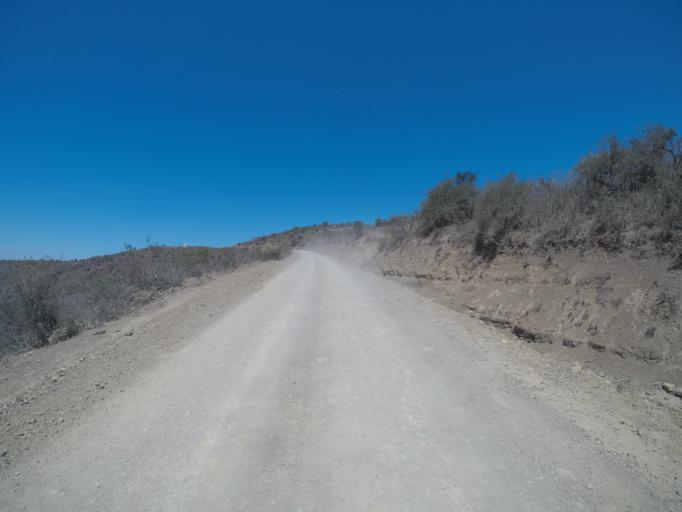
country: ZA
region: Eastern Cape
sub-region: OR Tambo District Municipality
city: Mthatha
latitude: -31.8765
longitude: 28.8733
